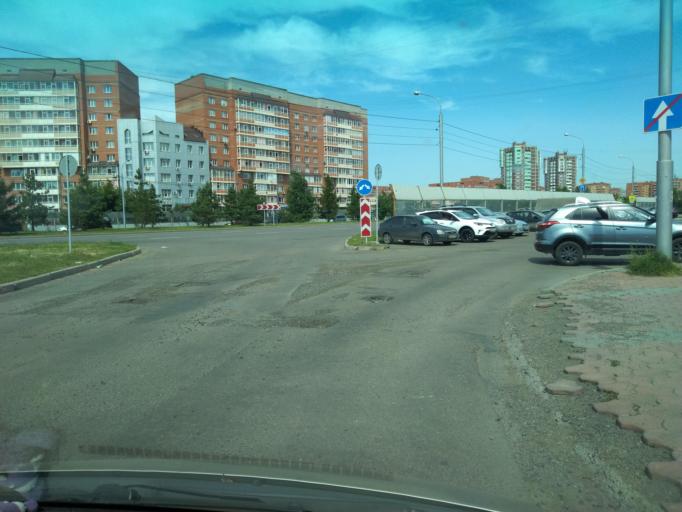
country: RU
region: Krasnoyarskiy
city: Krasnoyarsk
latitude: 56.0510
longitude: 92.9130
